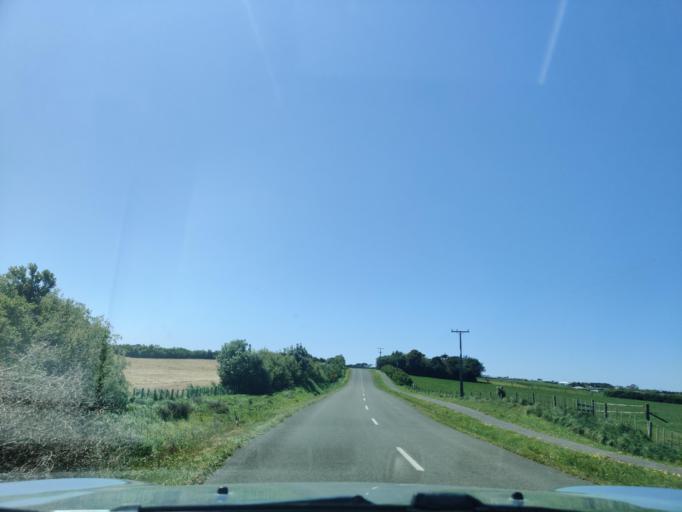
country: NZ
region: Taranaki
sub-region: South Taranaki District
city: Hawera
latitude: -39.6023
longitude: 174.2478
